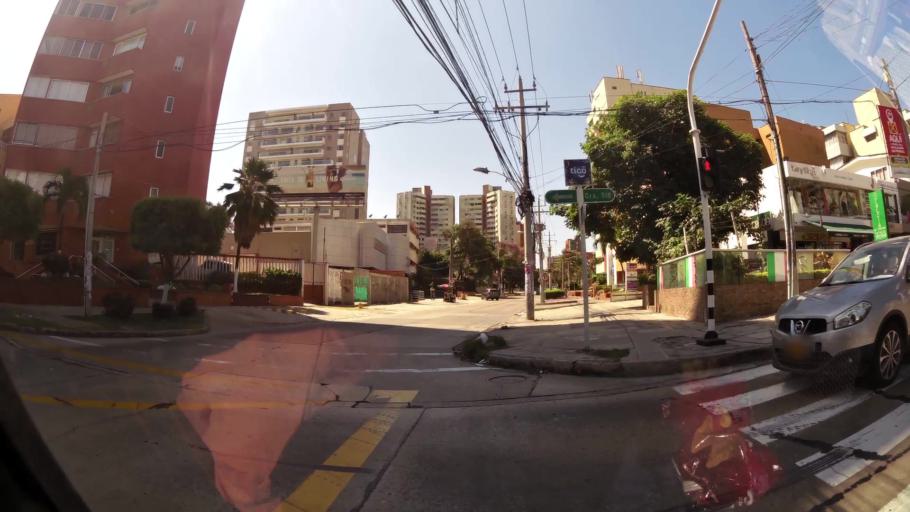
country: CO
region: Atlantico
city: Barranquilla
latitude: 11.0045
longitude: -74.8144
